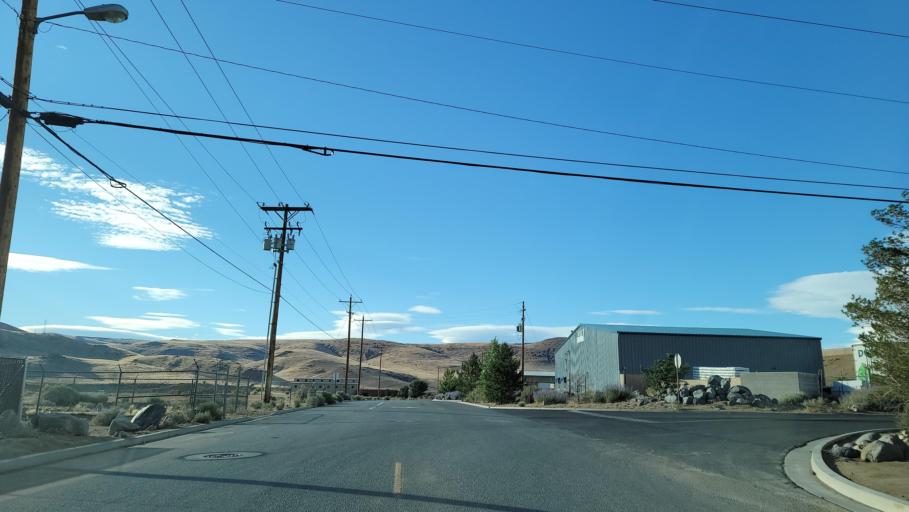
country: US
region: Nevada
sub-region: Washoe County
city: Spanish Springs
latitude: 39.5495
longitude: -119.5535
